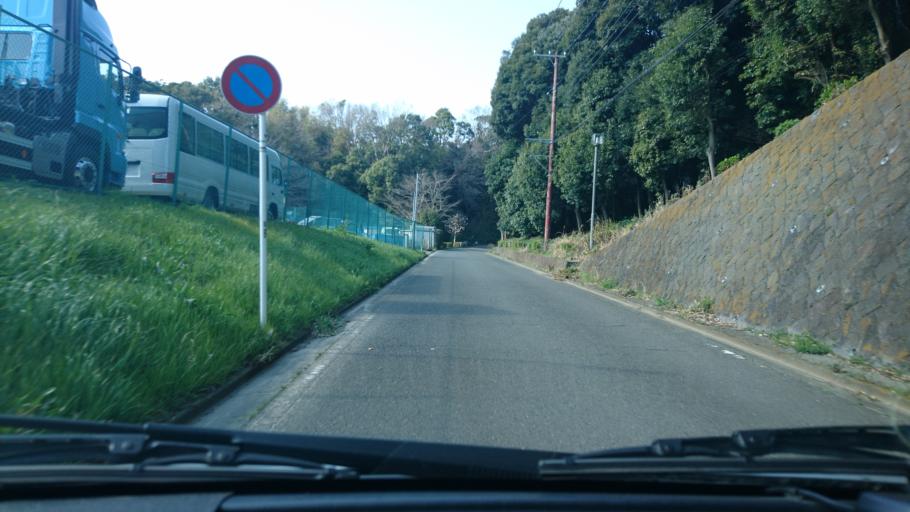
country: JP
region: Kanagawa
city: Fujisawa
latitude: 35.3854
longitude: 139.4249
